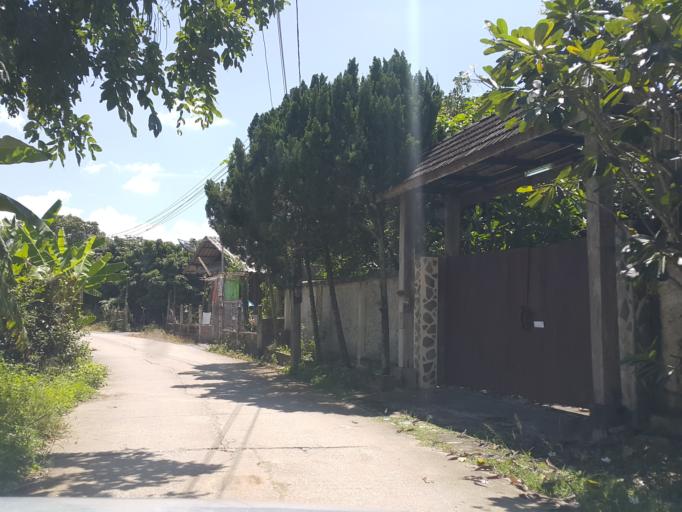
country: TH
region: Chiang Mai
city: San Kamphaeng
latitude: 18.6957
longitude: 99.1137
